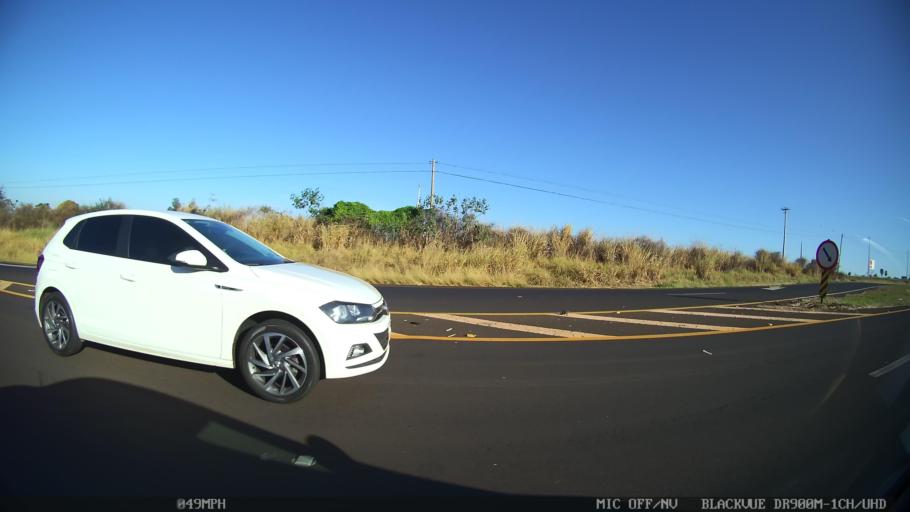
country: BR
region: Sao Paulo
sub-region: Olimpia
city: Olimpia
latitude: -20.7152
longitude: -48.9944
